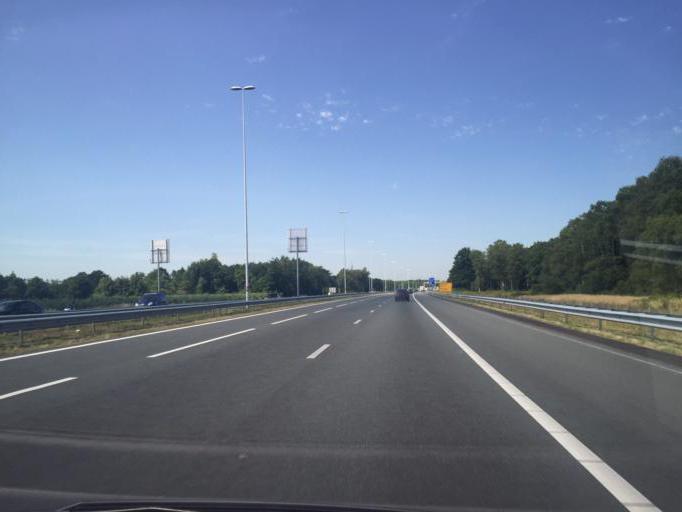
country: NL
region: Utrecht
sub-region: Gemeente Utrechtse Heuvelrug
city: Maarsbergen
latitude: 52.0527
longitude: 5.4183
